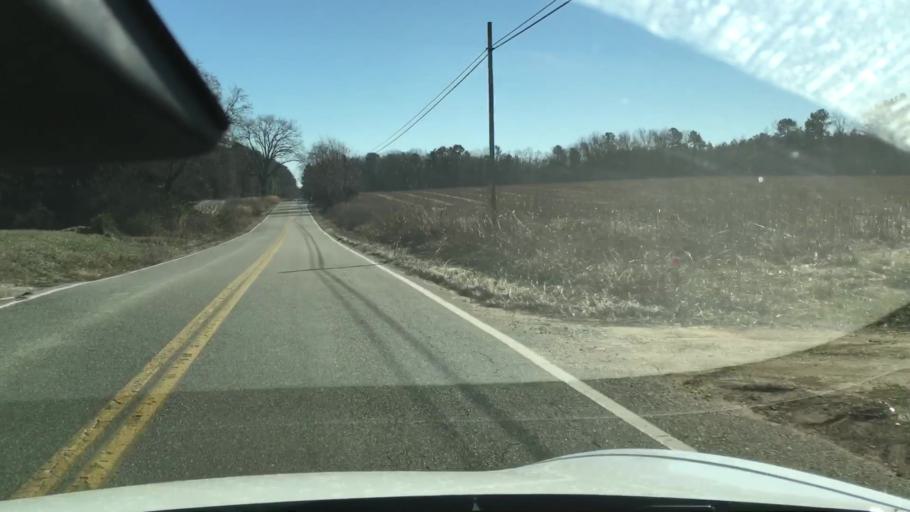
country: US
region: Virginia
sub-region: Henrico County
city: Short Pump
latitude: 37.5771
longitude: -77.7242
